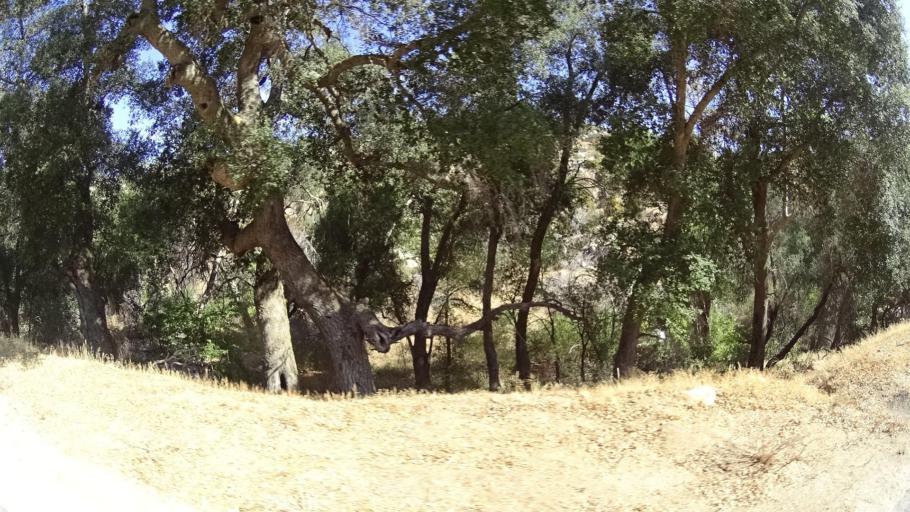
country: US
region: California
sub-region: Riverside County
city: Aguanga
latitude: 33.3723
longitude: -116.7099
